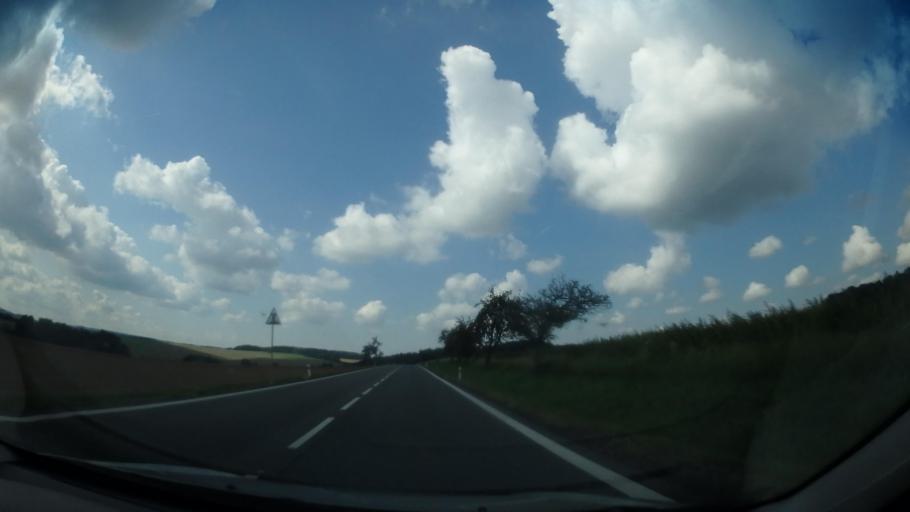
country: CZ
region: Central Bohemia
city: Kostelec nad Cernymi Lesy
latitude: 49.9735
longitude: 14.9051
